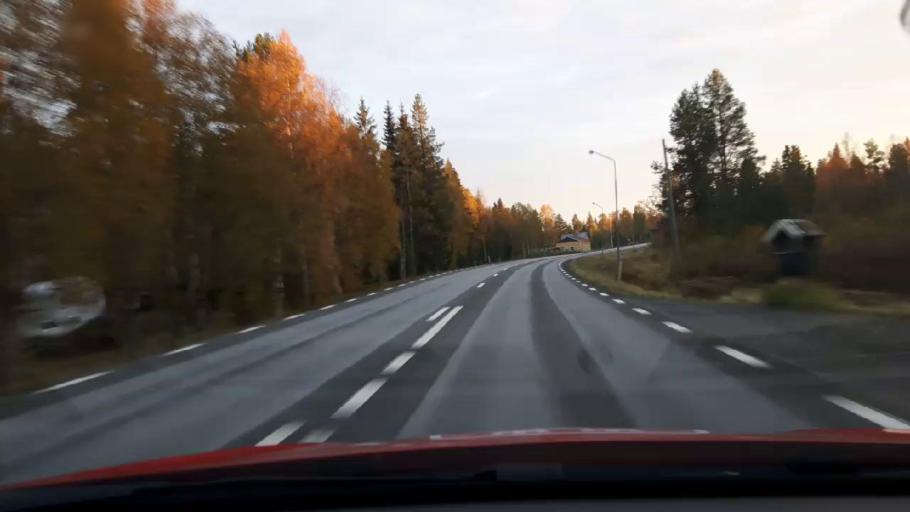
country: SE
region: Jaemtland
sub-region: OEstersunds Kommun
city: Lit
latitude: 63.2922
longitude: 14.8685
